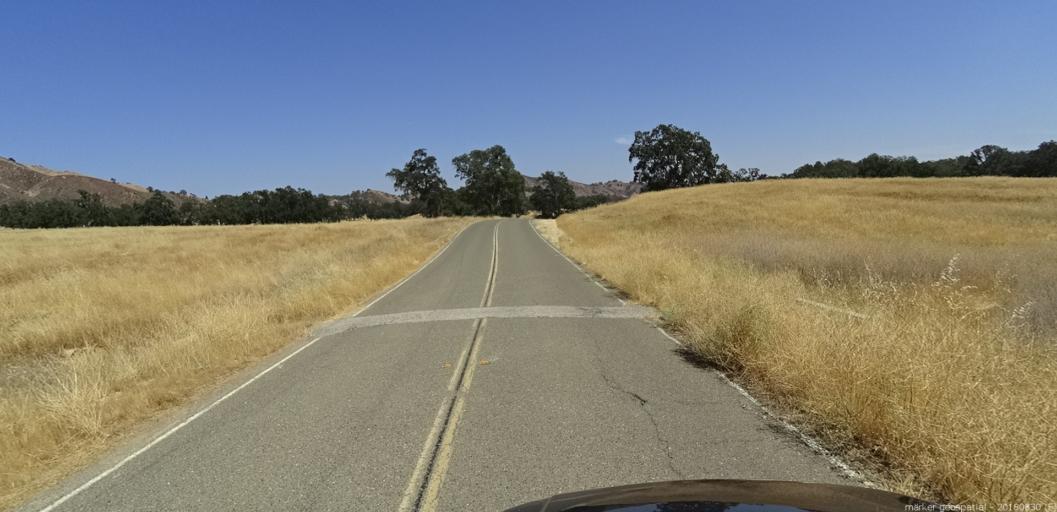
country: US
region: California
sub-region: Monterey County
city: King City
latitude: 35.9742
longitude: -121.3325
